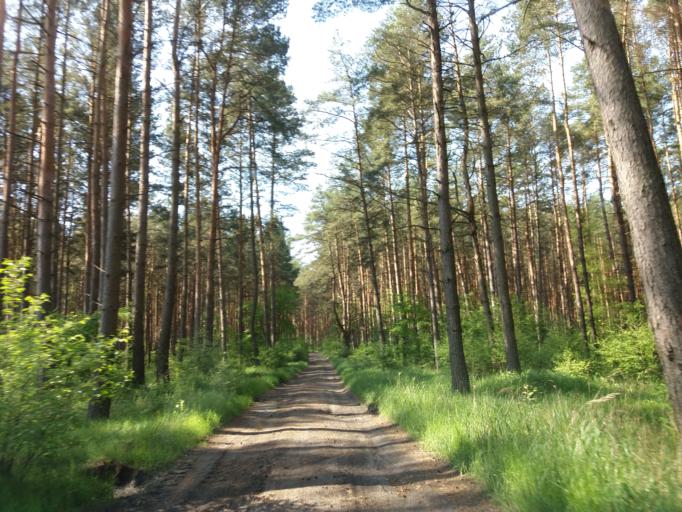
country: PL
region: West Pomeranian Voivodeship
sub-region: Powiat choszczenski
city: Bierzwnik
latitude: 53.1057
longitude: 15.6876
